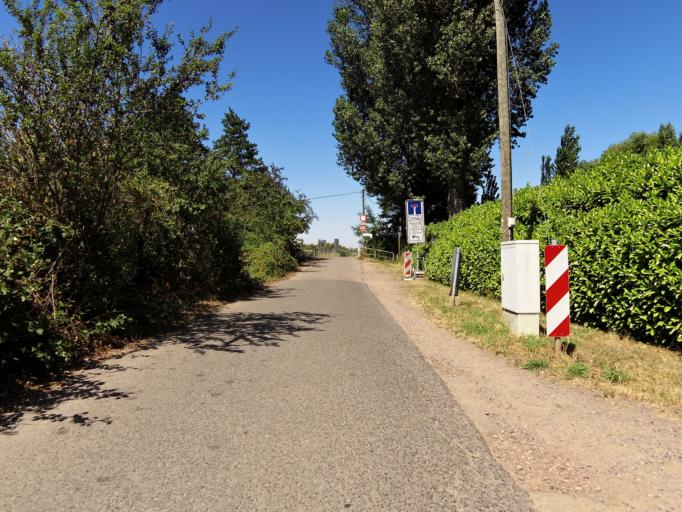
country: DE
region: Rheinland-Pfalz
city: Neustadt
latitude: 49.3559
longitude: 8.1676
